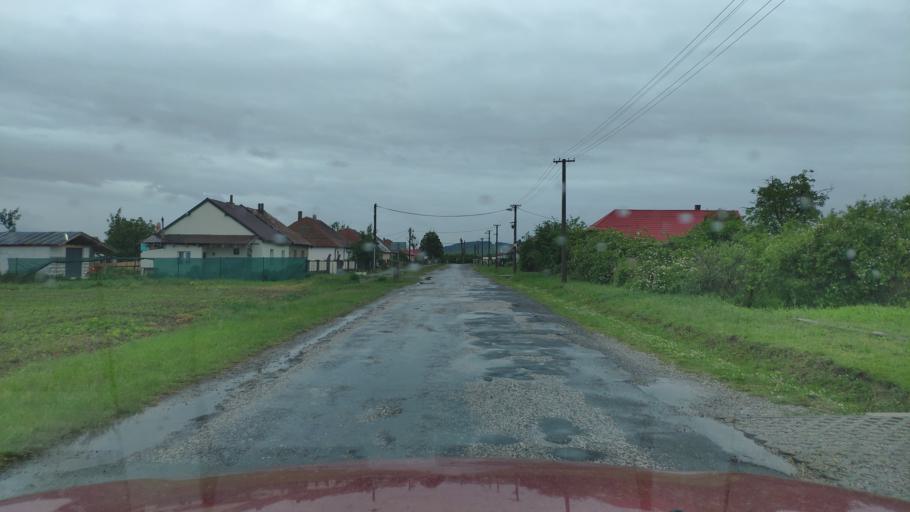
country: HU
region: Borsod-Abauj-Zemplen
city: Satoraljaujhely
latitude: 48.4220
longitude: 21.6767
